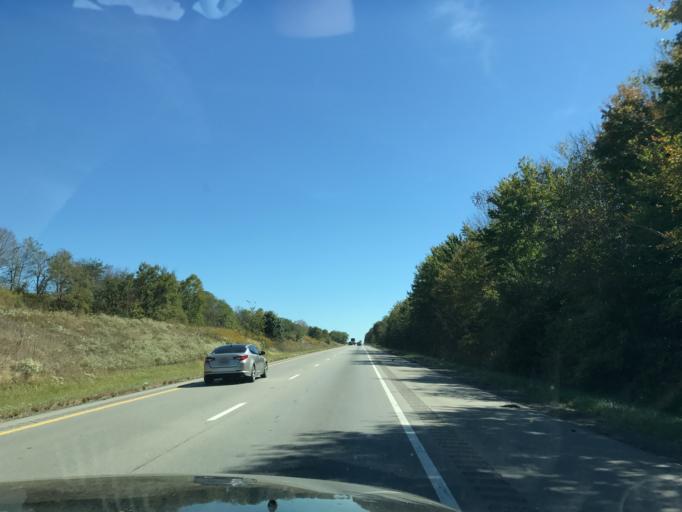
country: US
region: Ohio
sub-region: Muskingum County
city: Zanesville
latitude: 39.9510
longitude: -82.1757
